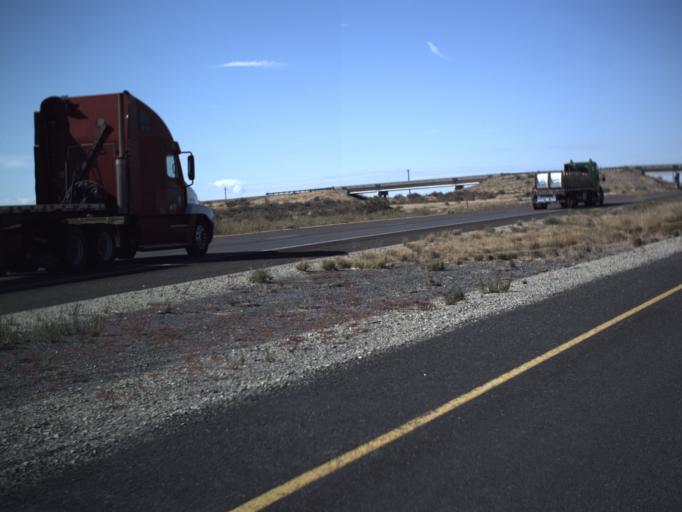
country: US
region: Utah
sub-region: Tooele County
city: Grantsville
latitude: 40.7337
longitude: -113.1097
